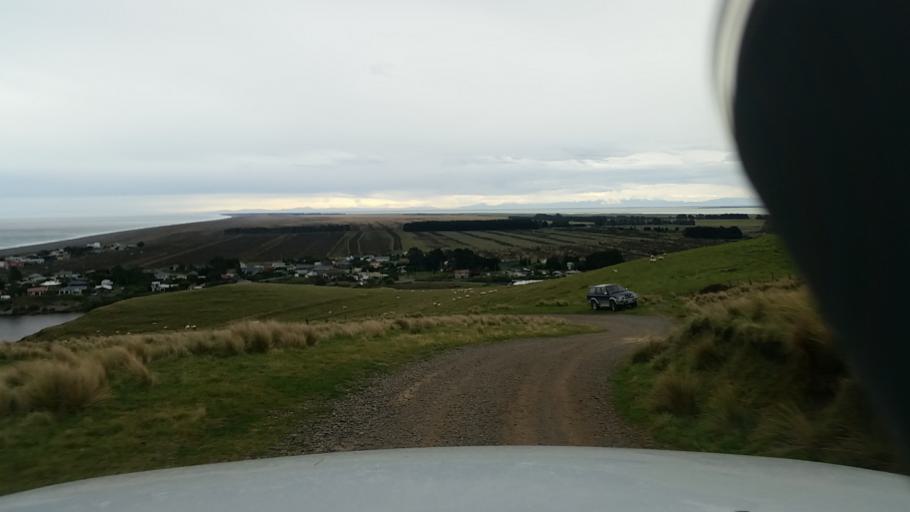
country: NZ
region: Canterbury
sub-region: Selwyn District
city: Lincoln
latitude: -43.8222
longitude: 172.7152
